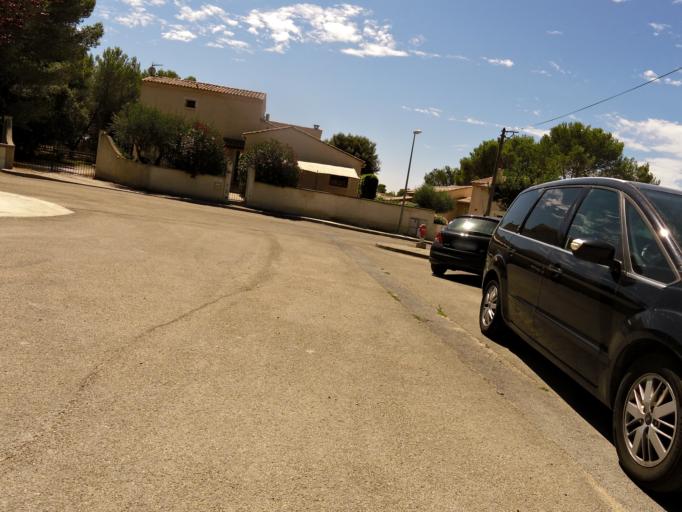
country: FR
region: Languedoc-Roussillon
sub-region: Departement du Gard
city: Vergeze
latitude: 43.7490
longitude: 4.2275
